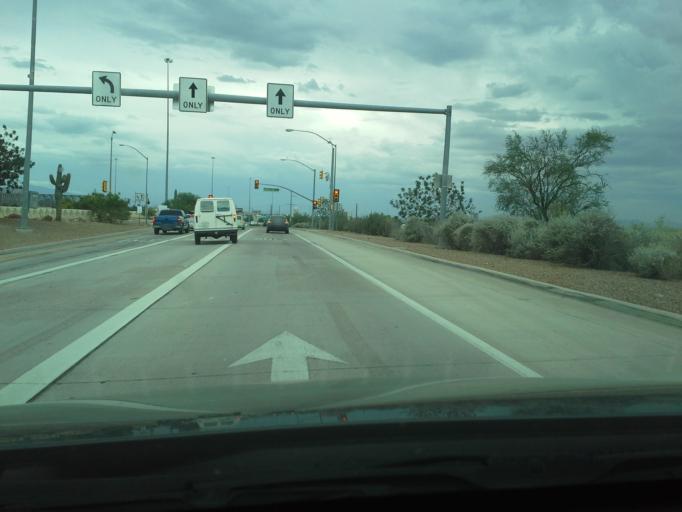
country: US
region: Arizona
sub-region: Pima County
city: Flowing Wells
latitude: 32.2604
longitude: -111.0040
